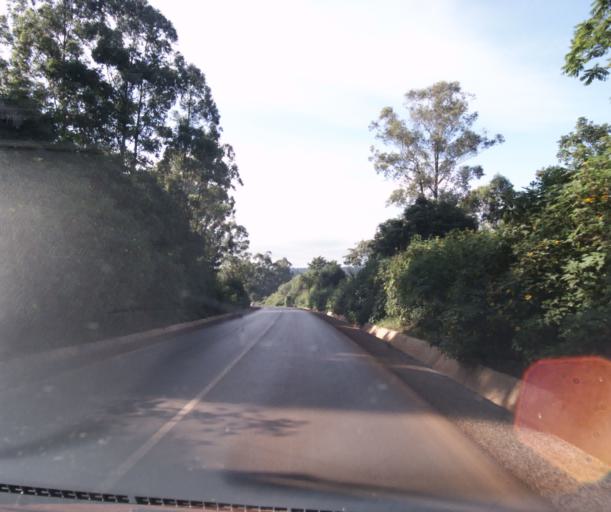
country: CM
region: West
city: Mbouda
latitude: 5.6087
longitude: 10.2889
